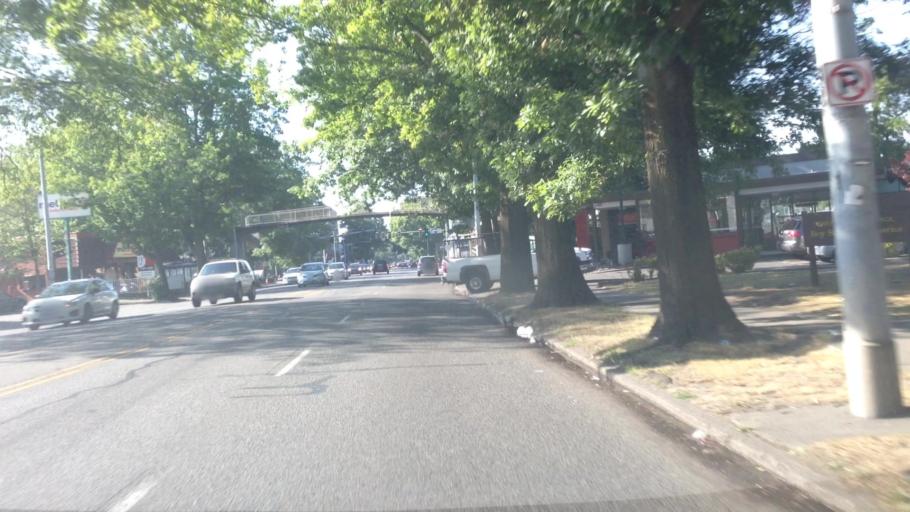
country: US
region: Washington
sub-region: King County
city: Seattle
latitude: 47.5751
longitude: -122.2955
